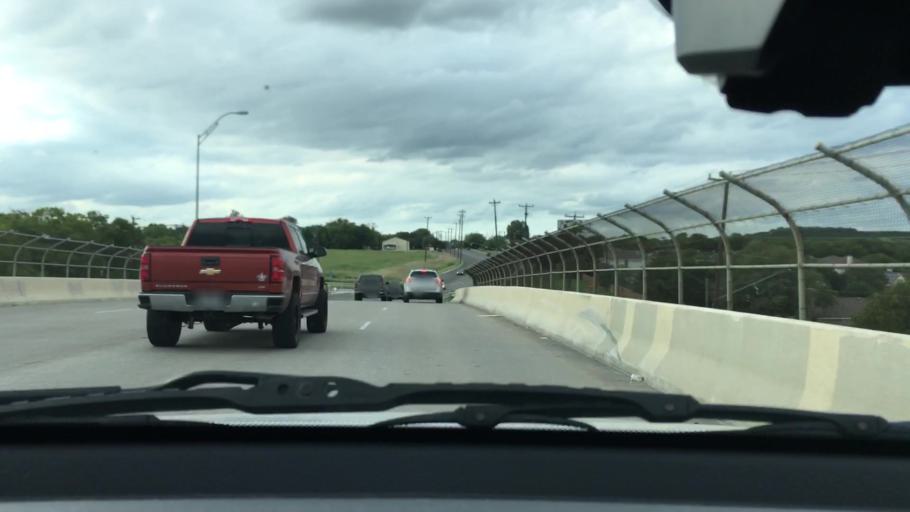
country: US
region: Texas
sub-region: Bexar County
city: Live Oak
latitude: 29.5678
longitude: -98.3660
